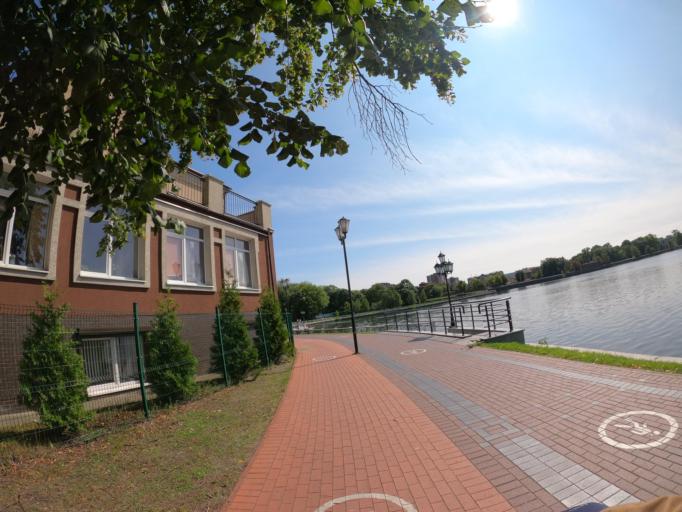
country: RU
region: Kaliningrad
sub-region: Gorod Kaliningrad
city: Kaliningrad
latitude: 54.7243
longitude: 20.5208
